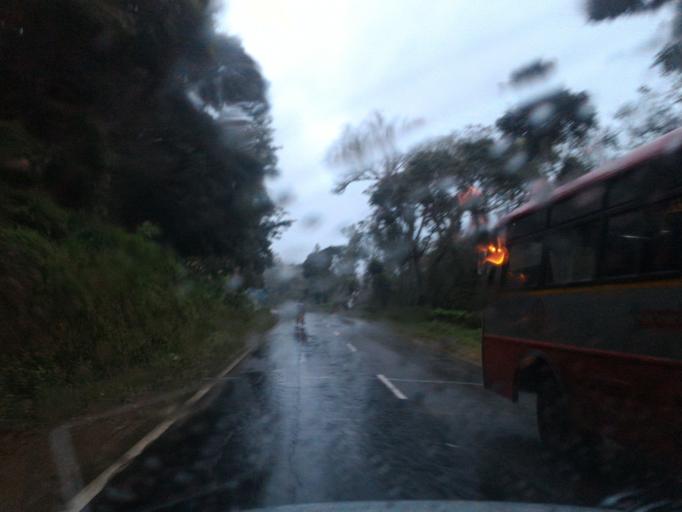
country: IN
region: Karnataka
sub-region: Kodagu
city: Suntikoppa
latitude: 12.4364
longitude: 75.8014
